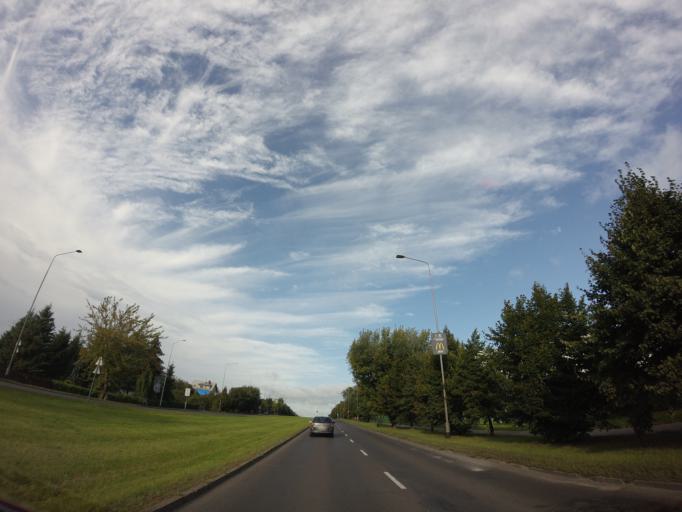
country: PL
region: West Pomeranian Voivodeship
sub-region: Szczecin
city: Szczecin
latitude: 53.4287
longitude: 14.5073
